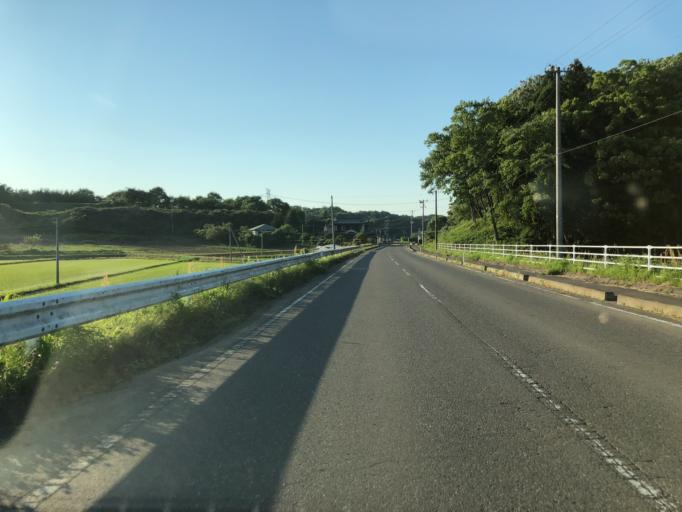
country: JP
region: Fukushima
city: Ishikawa
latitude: 37.0541
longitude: 140.4228
